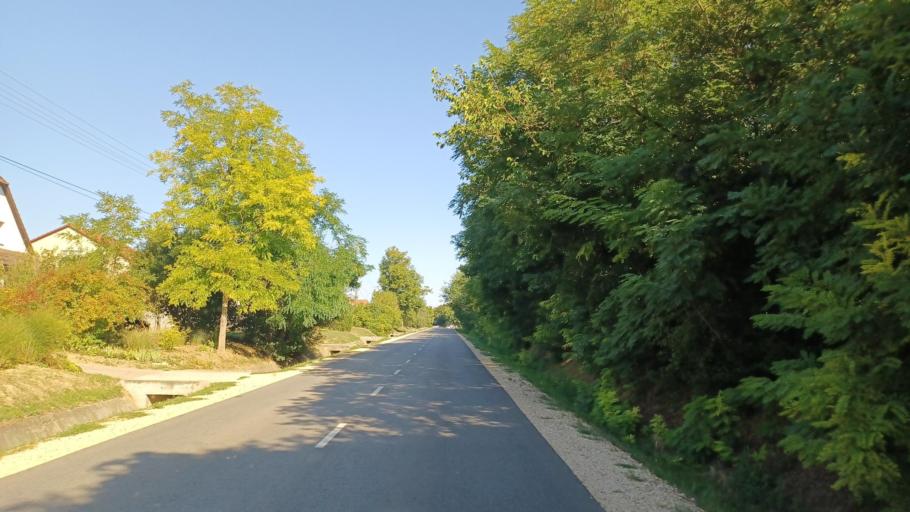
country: HU
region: Tolna
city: Nemetker
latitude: 46.6832
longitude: 18.8048
